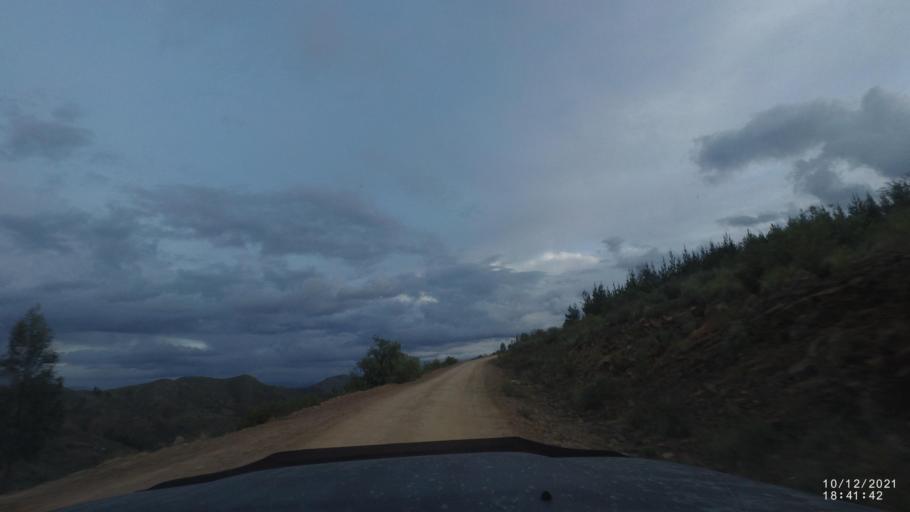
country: BO
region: Cochabamba
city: Tarata
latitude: -17.8639
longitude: -65.9874
